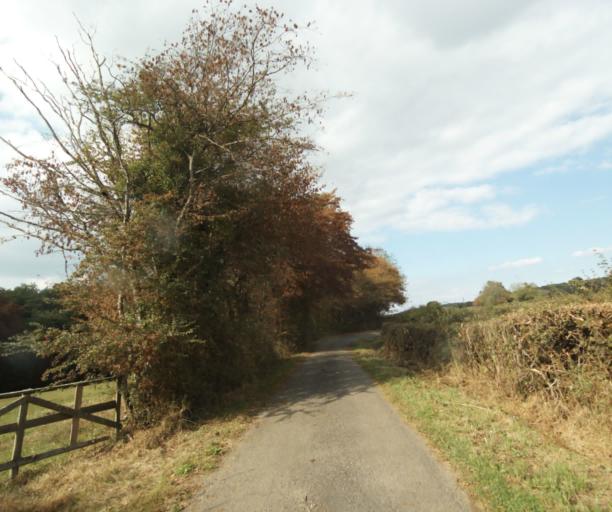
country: FR
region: Bourgogne
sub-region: Departement de Saone-et-Loire
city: Palinges
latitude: 46.5136
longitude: 4.2862
